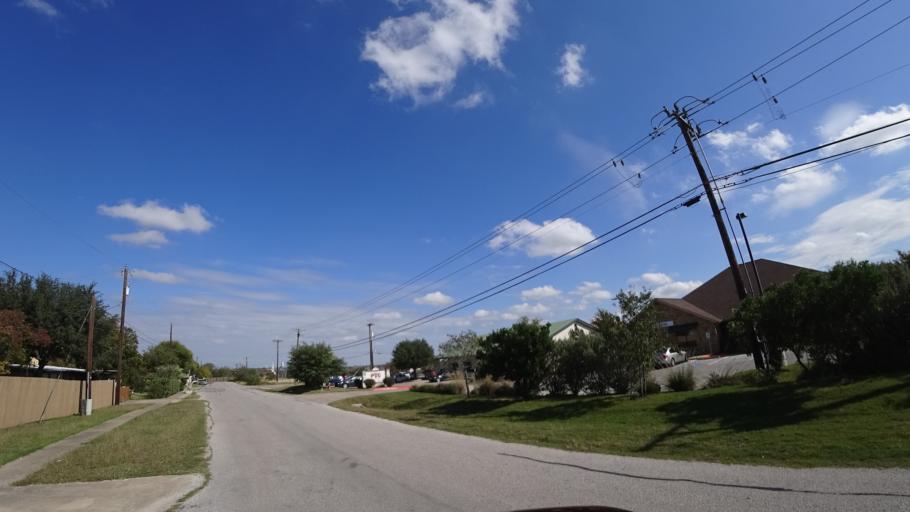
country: US
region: Texas
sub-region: Travis County
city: Windemere
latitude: 30.4500
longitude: -97.6402
